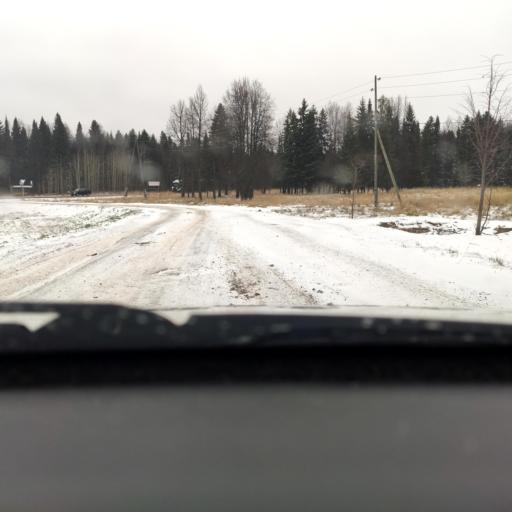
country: RU
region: Perm
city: Ferma
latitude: 57.9892
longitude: 56.3745
